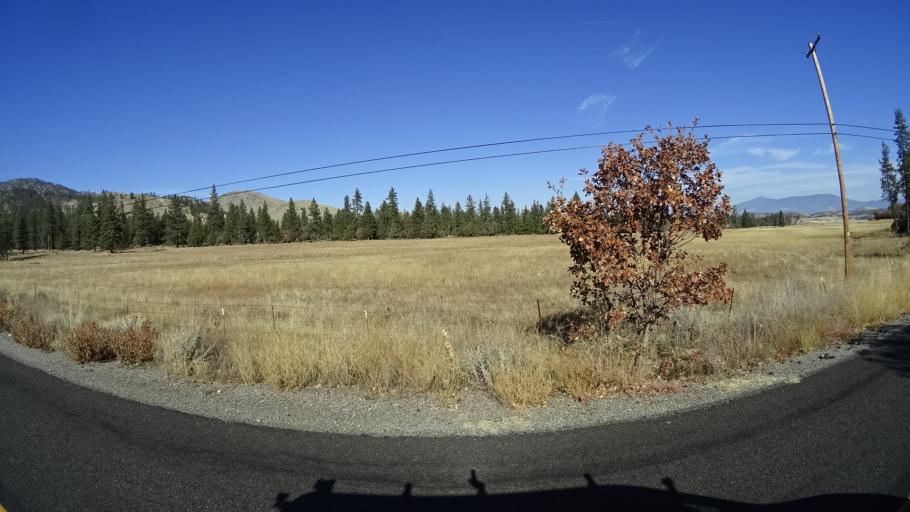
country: US
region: California
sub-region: Siskiyou County
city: Weed
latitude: 41.4356
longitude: -122.4604
